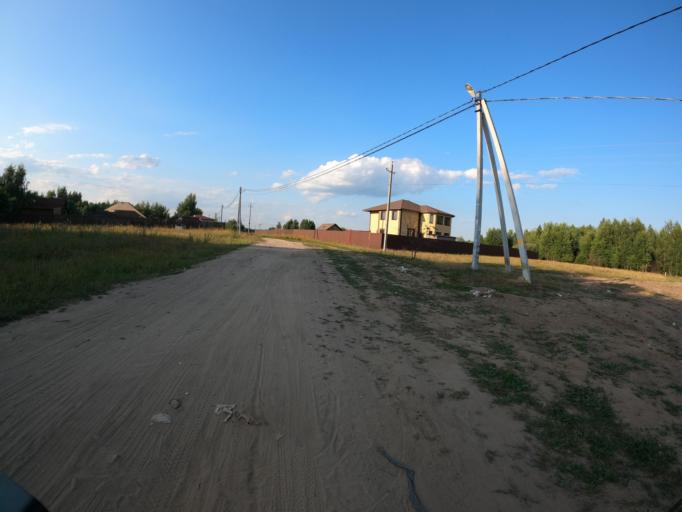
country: RU
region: Moskovskaya
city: Bronnitsy
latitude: 55.4808
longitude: 38.2581
